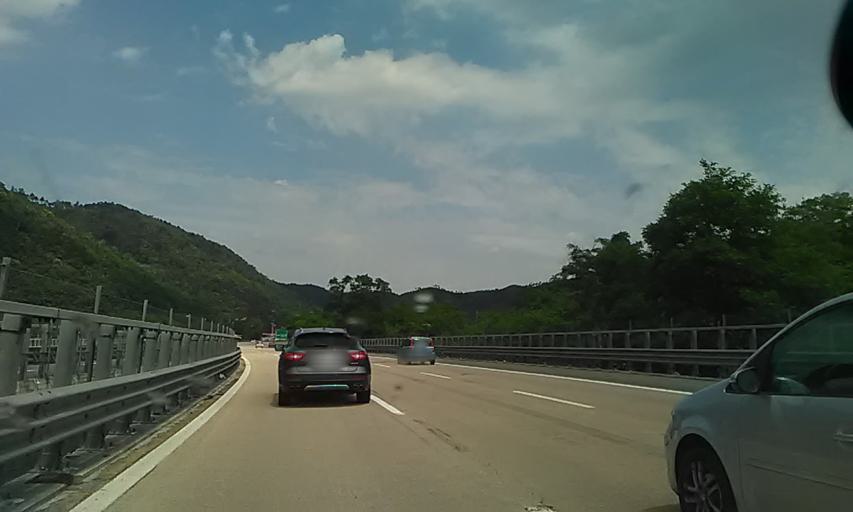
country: IT
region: Liguria
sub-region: Provincia di Genova
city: Rossiglione
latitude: 44.5865
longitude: 8.6651
